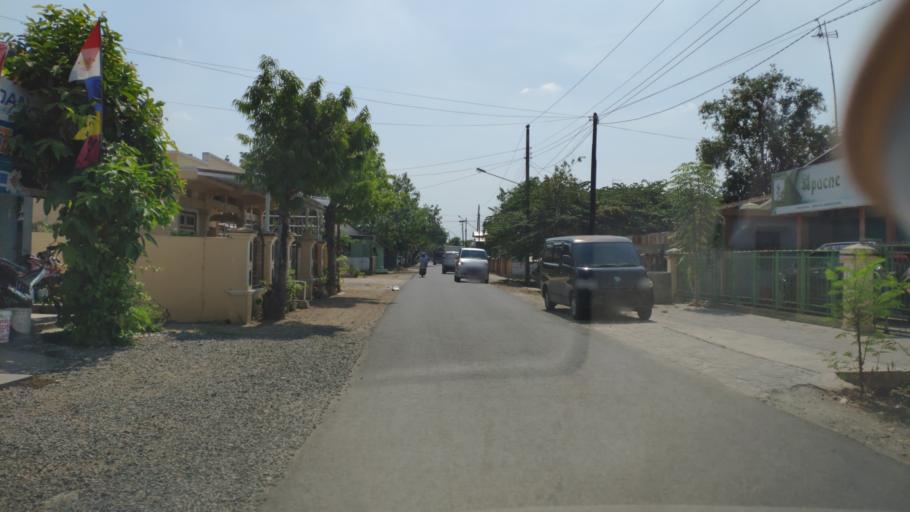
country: ID
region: Central Java
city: Kedungjenar
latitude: -6.9791
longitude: 111.4178
